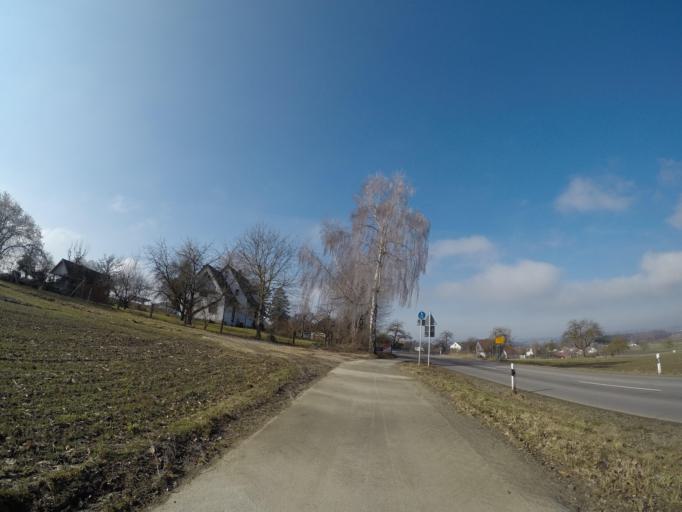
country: DE
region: Bavaria
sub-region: Swabia
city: Holzheim
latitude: 48.3831
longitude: 10.0813
